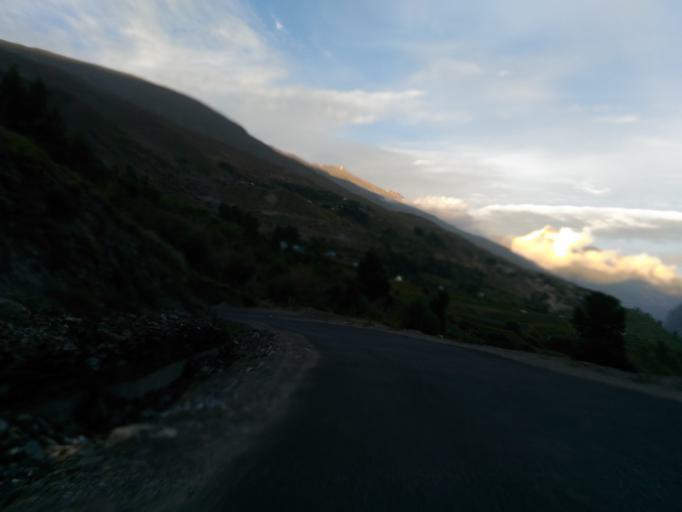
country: IN
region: Himachal Pradesh
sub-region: Lahul and Spiti
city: Kyelang
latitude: 32.5114
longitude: 77.0074
